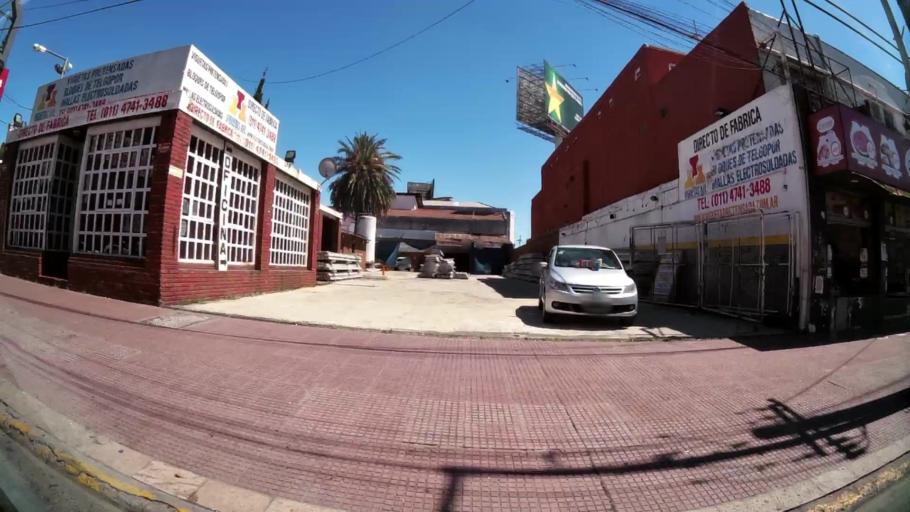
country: AR
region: Buenos Aires
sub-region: Partido de Tigre
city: Tigre
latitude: -34.4862
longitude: -58.6165
